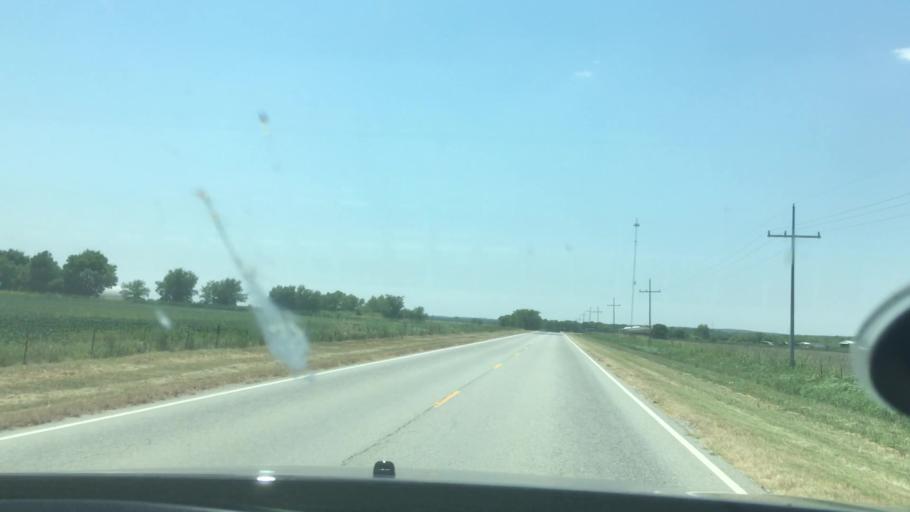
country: US
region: Oklahoma
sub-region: Coal County
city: Coalgate
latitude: 34.4934
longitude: -96.4164
